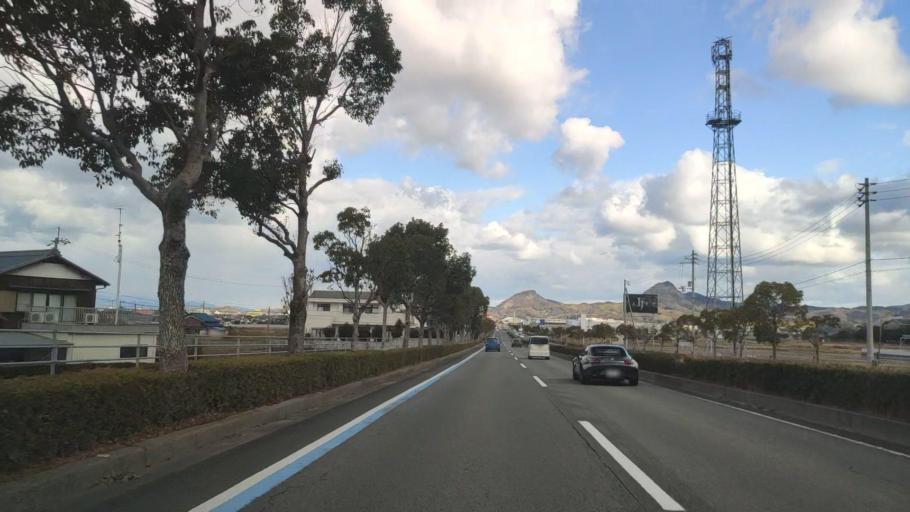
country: JP
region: Ehime
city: Hojo
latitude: 33.9552
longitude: 132.7758
